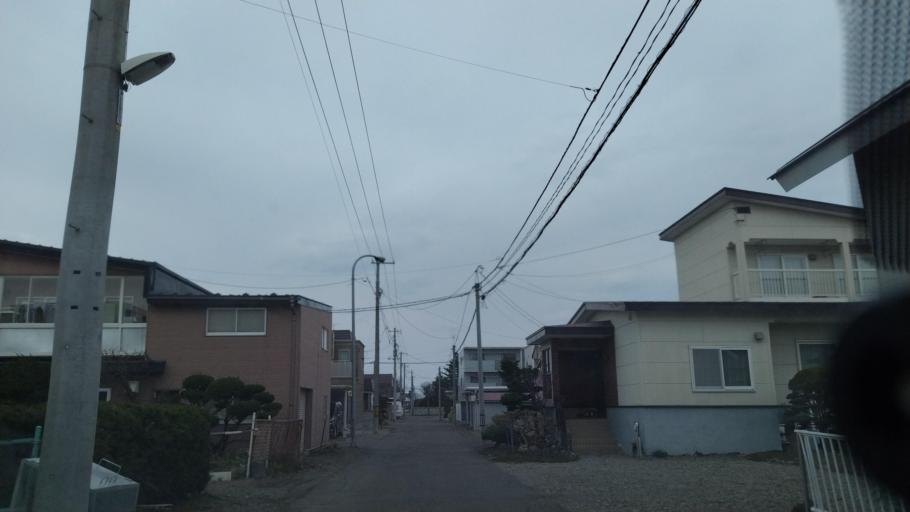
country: JP
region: Hokkaido
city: Obihiro
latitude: 42.9212
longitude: 143.2202
